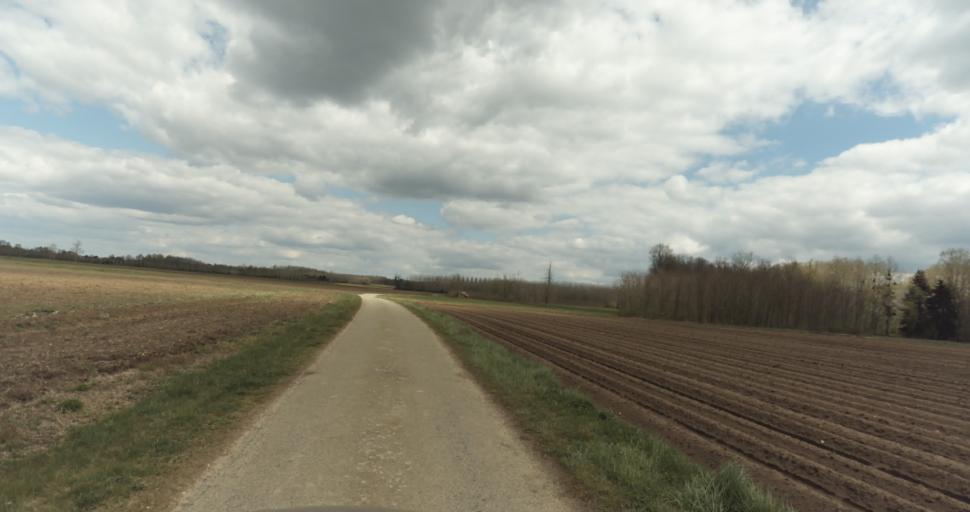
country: FR
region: Bourgogne
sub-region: Departement de la Cote-d'Or
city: Auxonne
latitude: 47.1598
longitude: 5.3894
